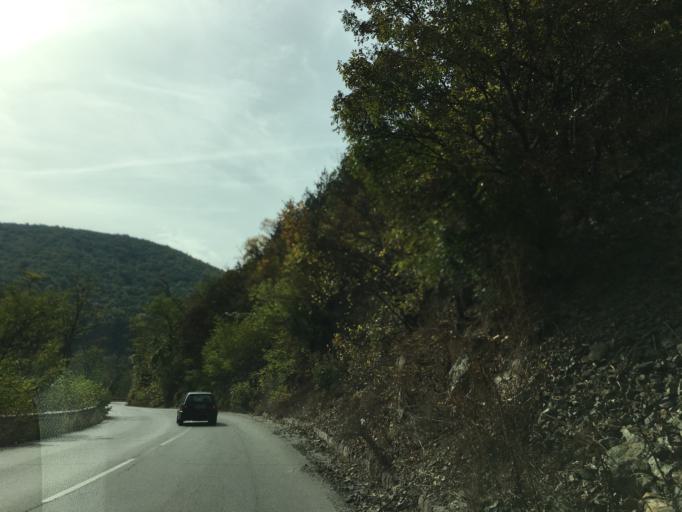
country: BG
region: Sofia-Capital
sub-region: Stolichna Obshtina
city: Sofia
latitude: 42.5703
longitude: 23.4320
